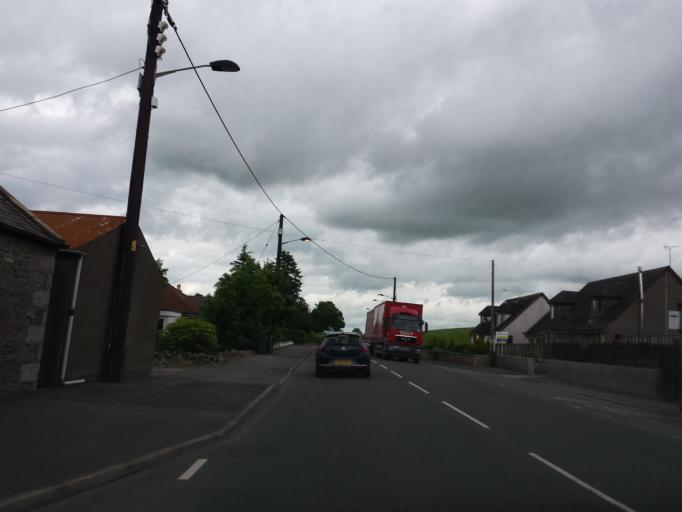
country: GB
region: Scotland
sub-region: Dumfries and Galloway
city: Dalbeattie
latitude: 55.0360
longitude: -3.8285
